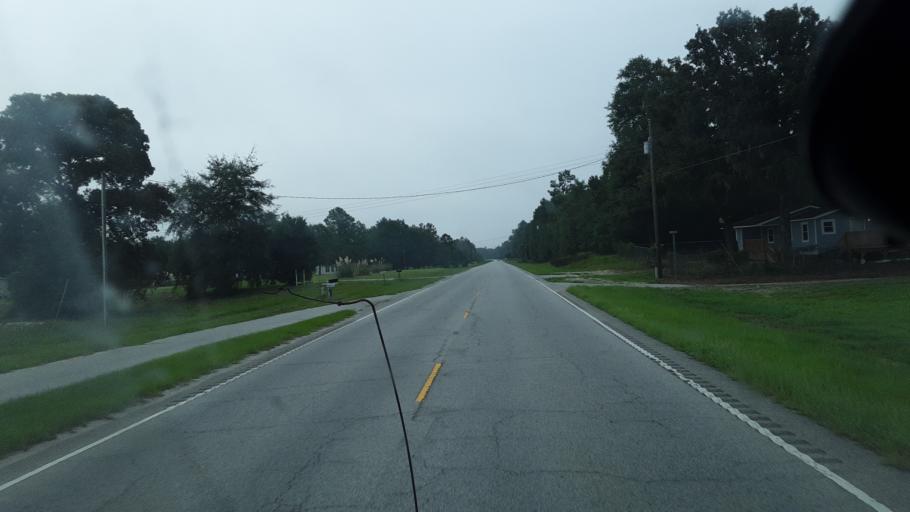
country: US
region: South Carolina
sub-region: Florence County
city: Johnsonville
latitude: 33.9033
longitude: -79.3978
